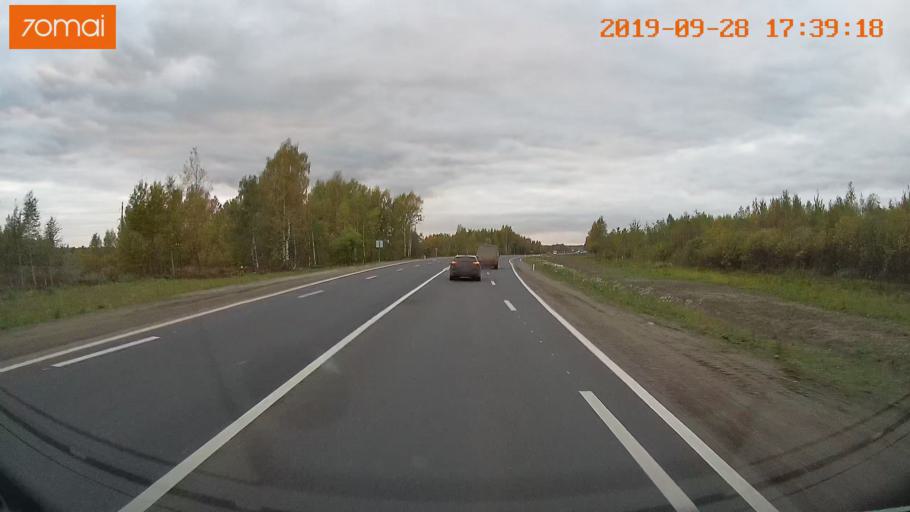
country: RU
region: Jaroslavl
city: Yaroslavl
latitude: 57.5442
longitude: 39.9236
